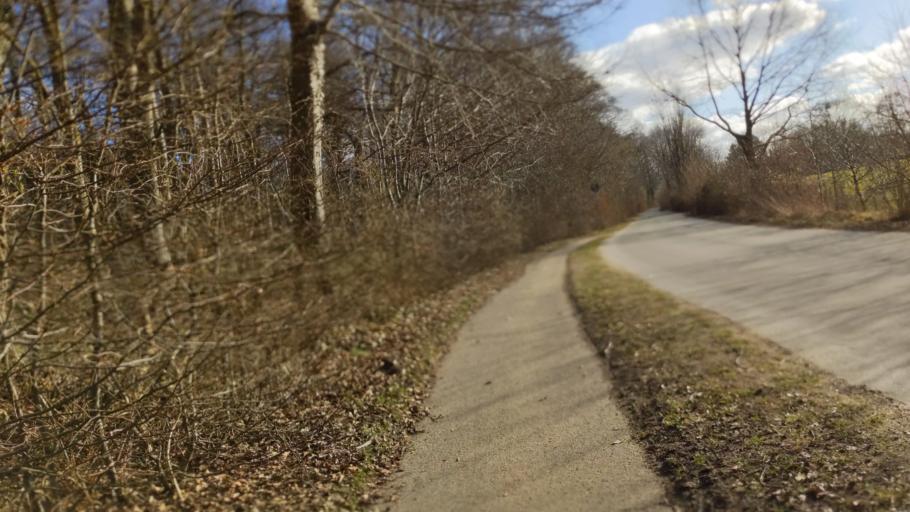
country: DE
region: Schleswig-Holstein
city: Timmendorfer Strand
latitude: 54.0057
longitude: 10.7549
